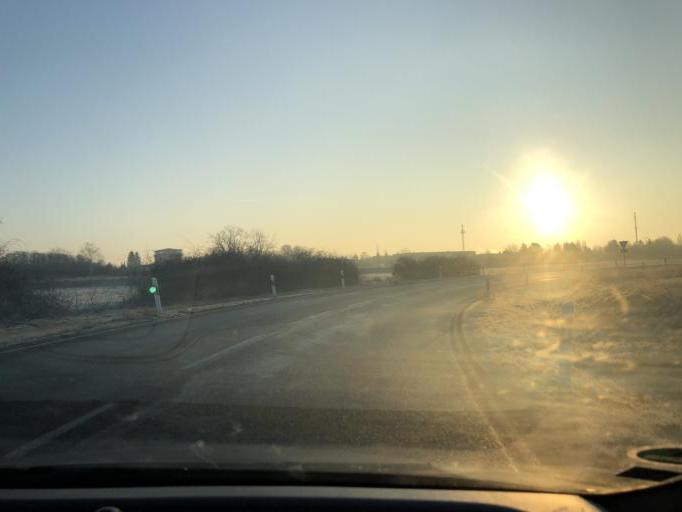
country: DE
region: Saxony
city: Schkeuditz
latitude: 51.4046
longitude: 12.2041
